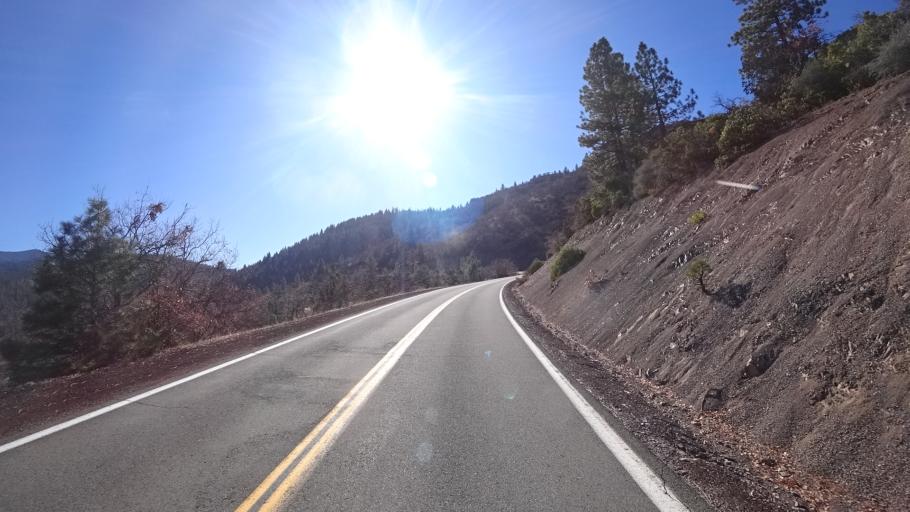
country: US
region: California
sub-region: Siskiyou County
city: Weed
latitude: 41.4496
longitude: -122.6466
